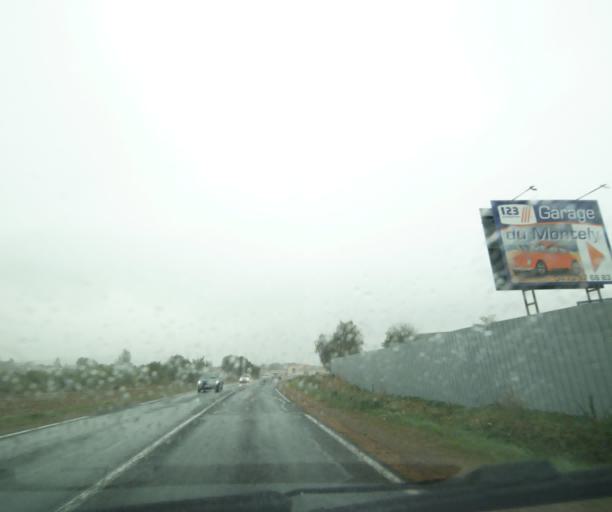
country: FR
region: Auvergne
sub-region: Departement du Puy-de-Dome
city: Blanzat
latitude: 45.8342
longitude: 3.0880
